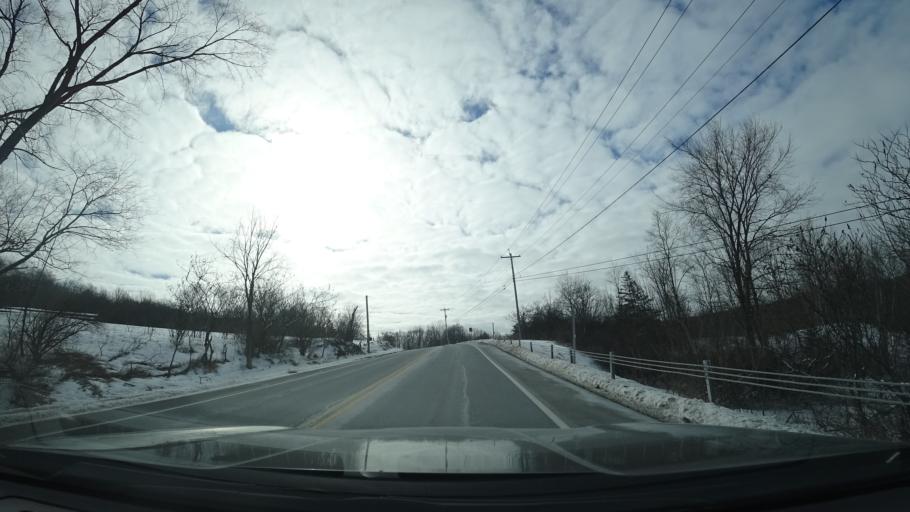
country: US
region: New York
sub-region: Washington County
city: Fort Edward
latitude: 43.2528
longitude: -73.5023
